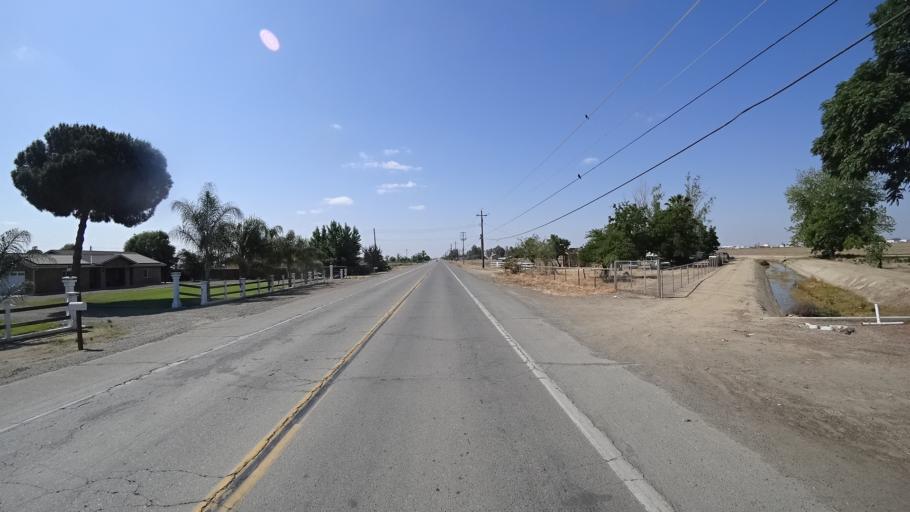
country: US
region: California
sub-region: Kings County
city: Home Garden
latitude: 36.2839
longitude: -119.6370
